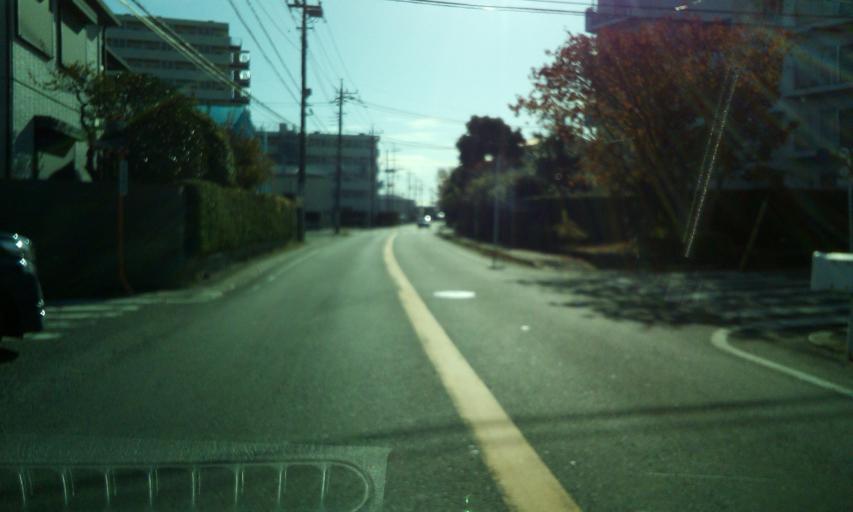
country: JP
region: Chiba
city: Nagareyama
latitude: 35.8597
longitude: 139.8881
